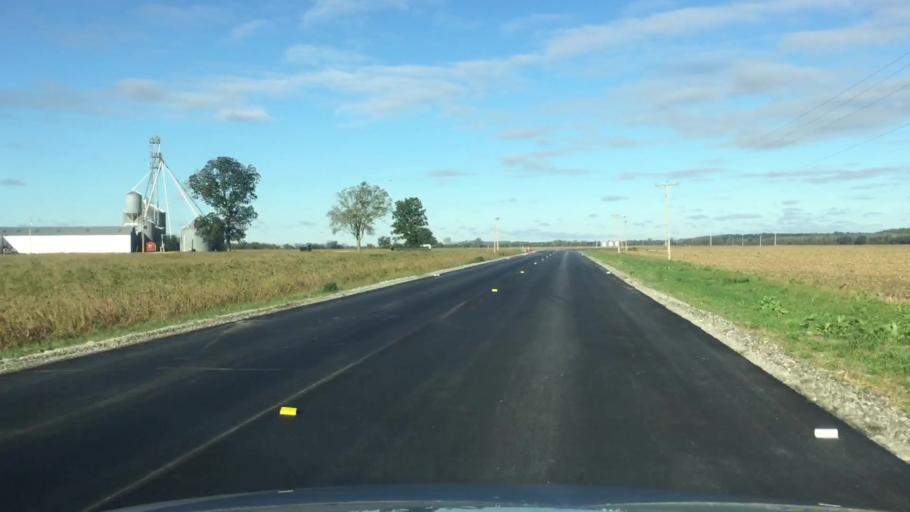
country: US
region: Missouri
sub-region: Howard County
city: New Franklin
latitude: 38.9967
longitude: -92.6673
